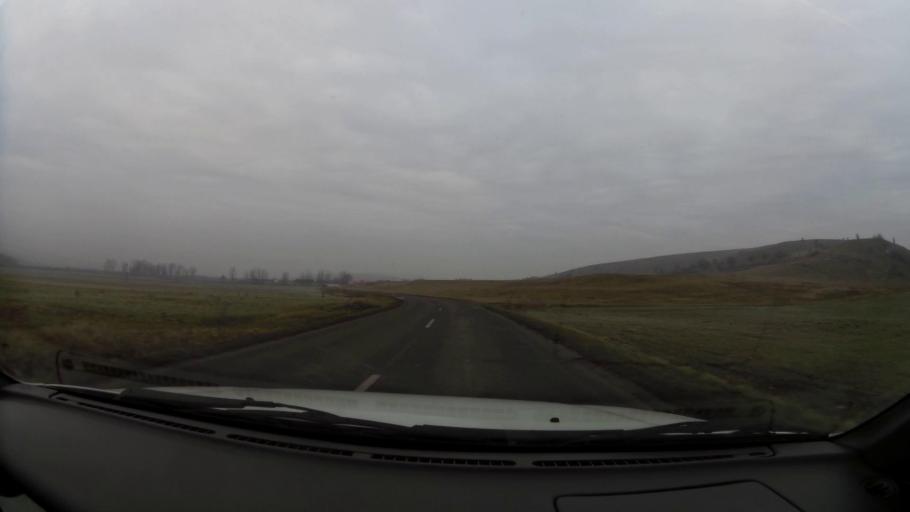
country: HU
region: Borsod-Abauj-Zemplen
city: Izsofalva
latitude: 48.2931
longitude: 20.6605
